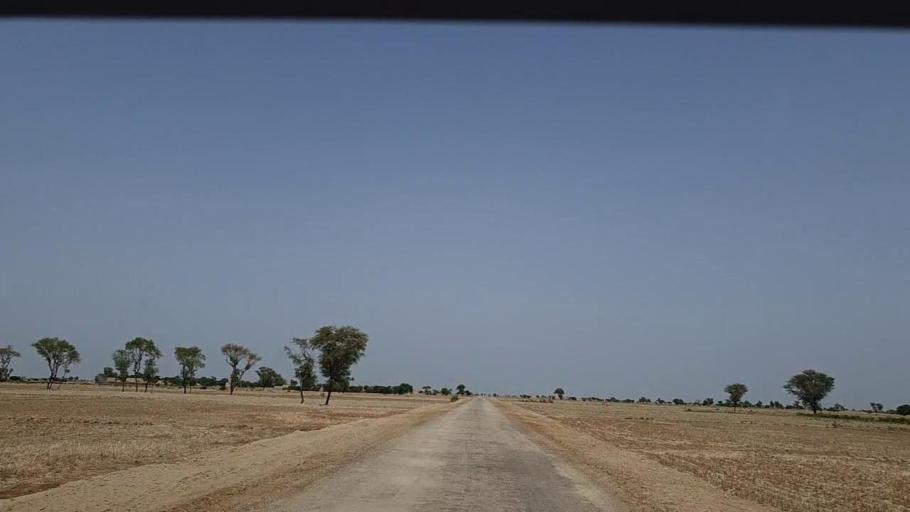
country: PK
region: Sindh
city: Johi
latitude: 26.7705
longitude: 67.6294
